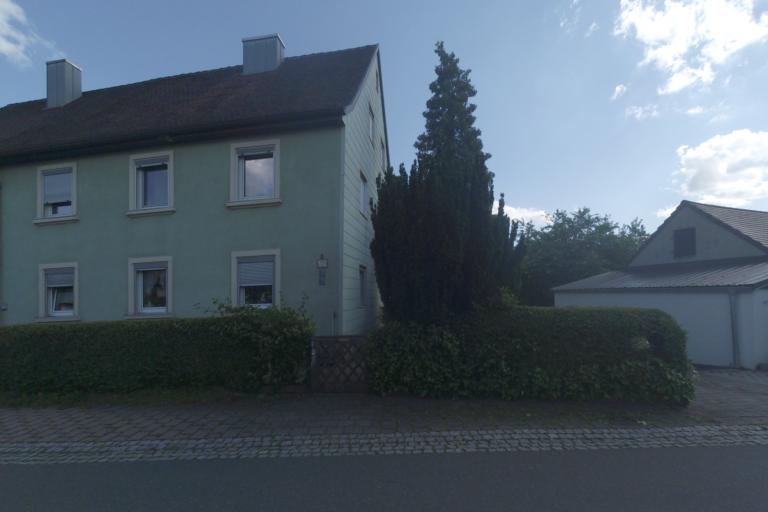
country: DE
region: Bavaria
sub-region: Regierungsbezirk Mittelfranken
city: Hagenbuchach
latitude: 49.5235
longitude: 10.7487
